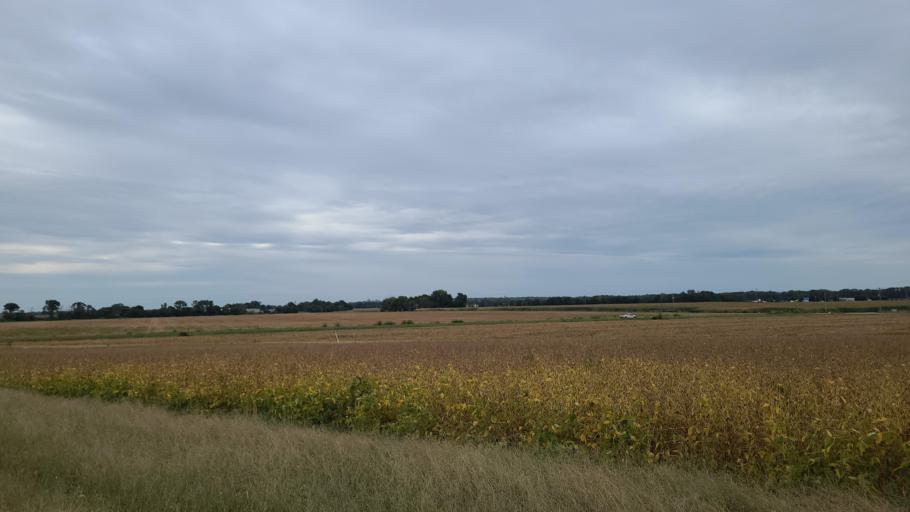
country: US
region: Kansas
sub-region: Douglas County
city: Lawrence
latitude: 39.0169
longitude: -95.2214
